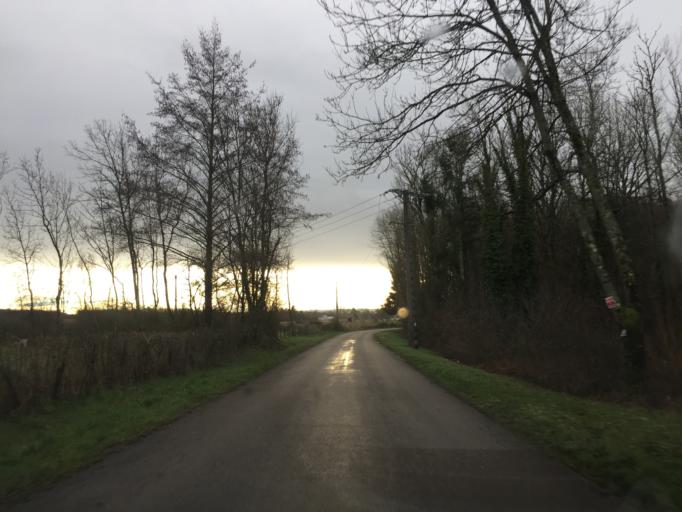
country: FR
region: Franche-Comte
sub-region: Departement du Jura
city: Choisey
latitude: 47.0449
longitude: 5.5068
